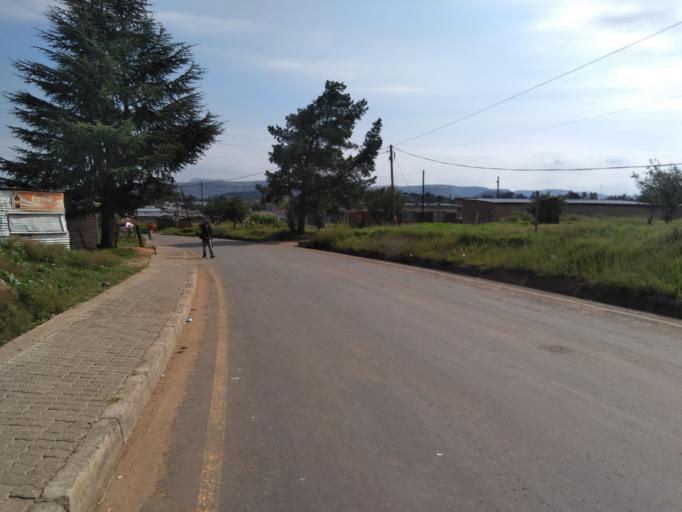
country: LS
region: Butha-Buthe
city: Butha-Buthe
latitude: -28.7709
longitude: 28.2502
